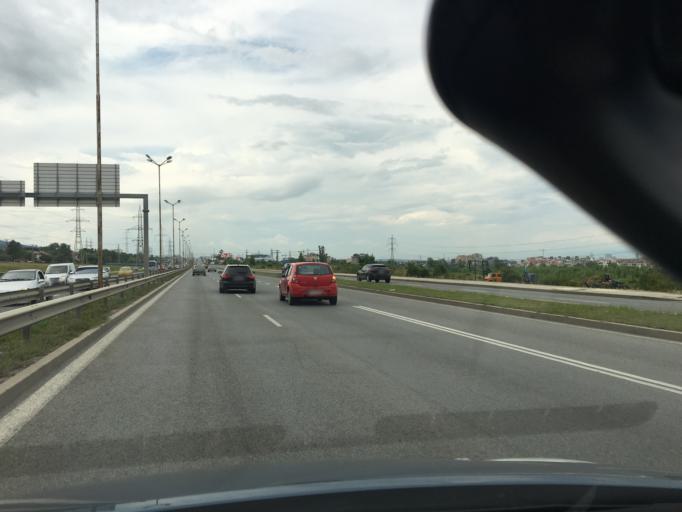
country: BG
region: Sofia-Capital
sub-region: Stolichna Obshtina
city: Sofia
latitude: 42.6285
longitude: 23.3448
